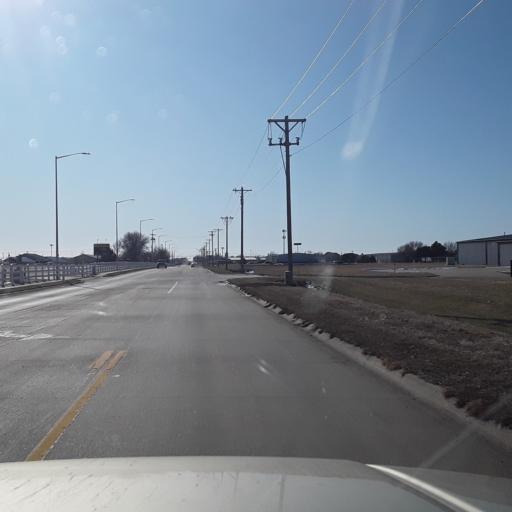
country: US
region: Nebraska
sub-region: Adams County
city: Hastings
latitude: 40.5743
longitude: -98.4021
